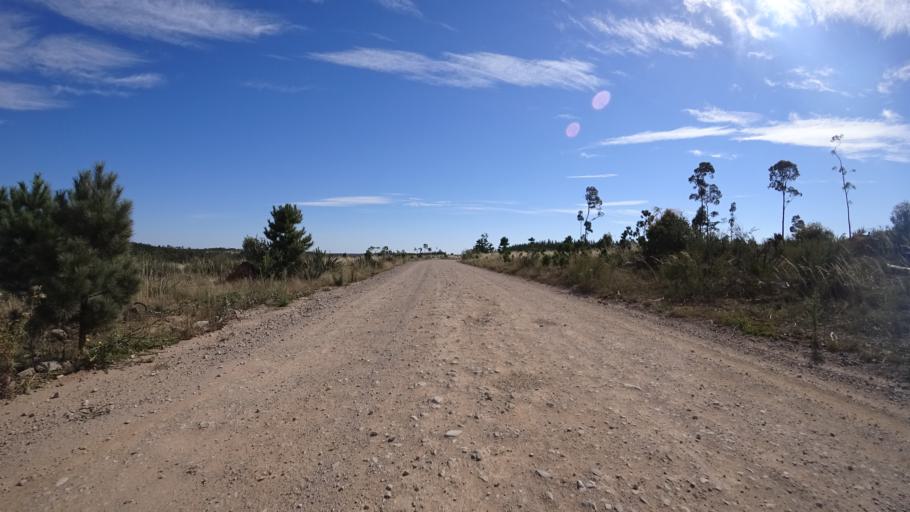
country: AU
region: New South Wales
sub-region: Lithgow
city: Lithgow
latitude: -33.3780
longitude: 150.2433
